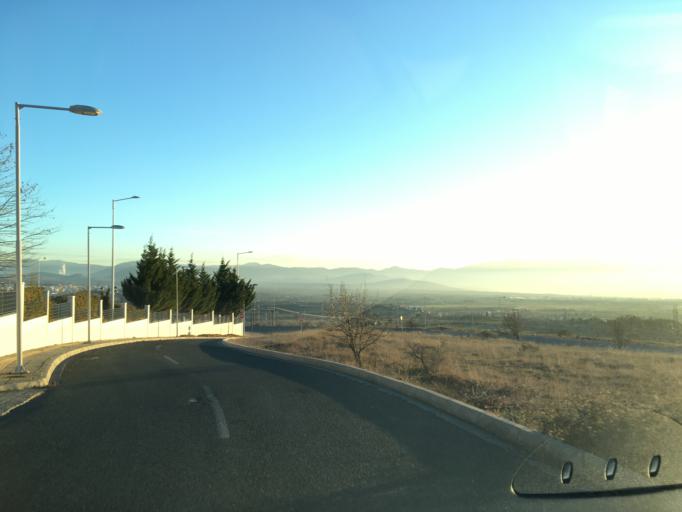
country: GR
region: West Macedonia
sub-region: Nomos Kozanis
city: Kozani
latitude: 40.2709
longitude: 21.7568
